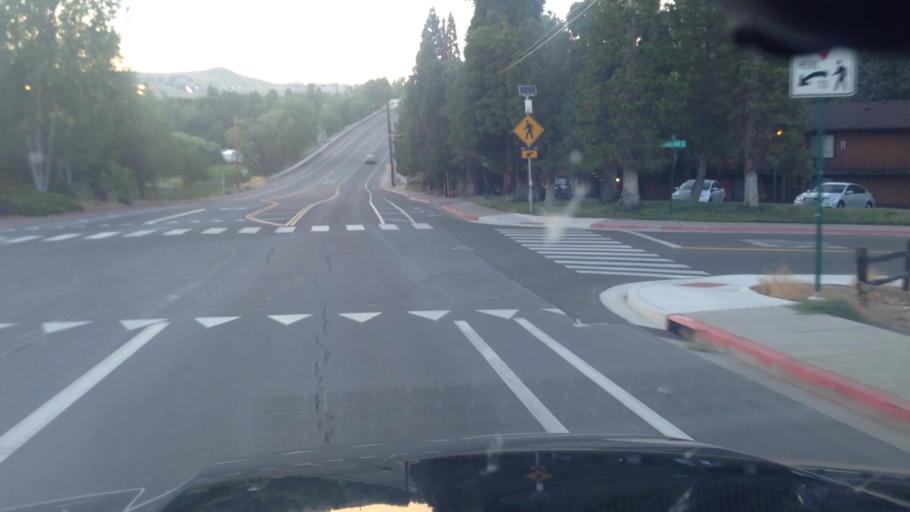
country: US
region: Nevada
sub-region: Washoe County
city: Reno
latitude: 39.5444
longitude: -119.8212
